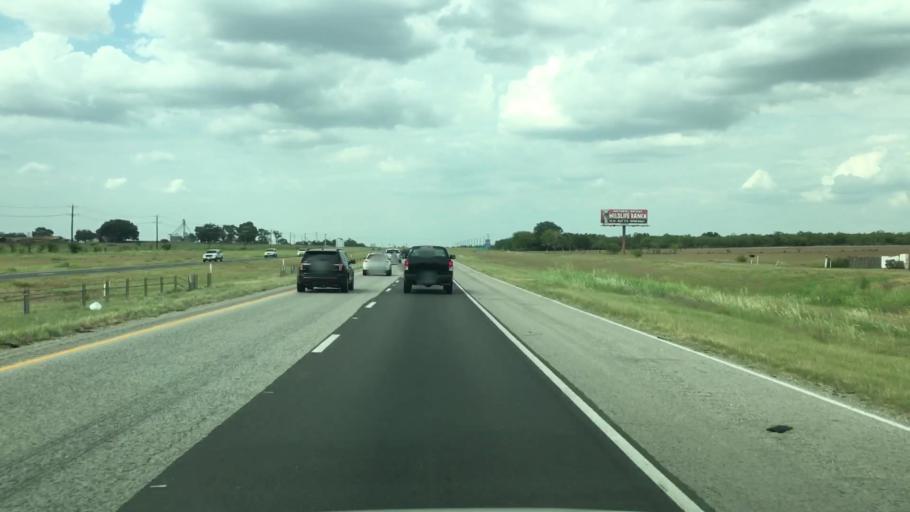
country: US
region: Texas
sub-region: Atascosa County
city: Pleasanton
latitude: 29.0017
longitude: -98.4310
